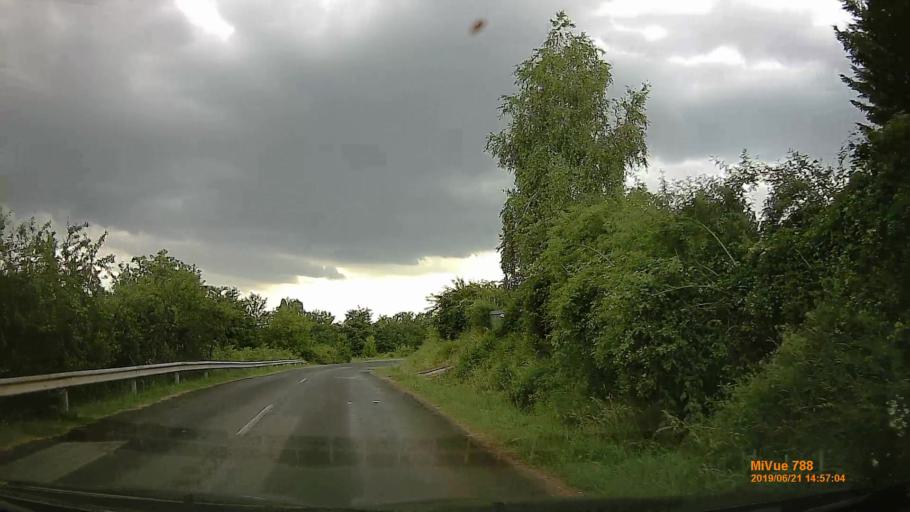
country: HU
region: Baranya
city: Hosszuheteny
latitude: 46.1098
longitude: 18.3136
